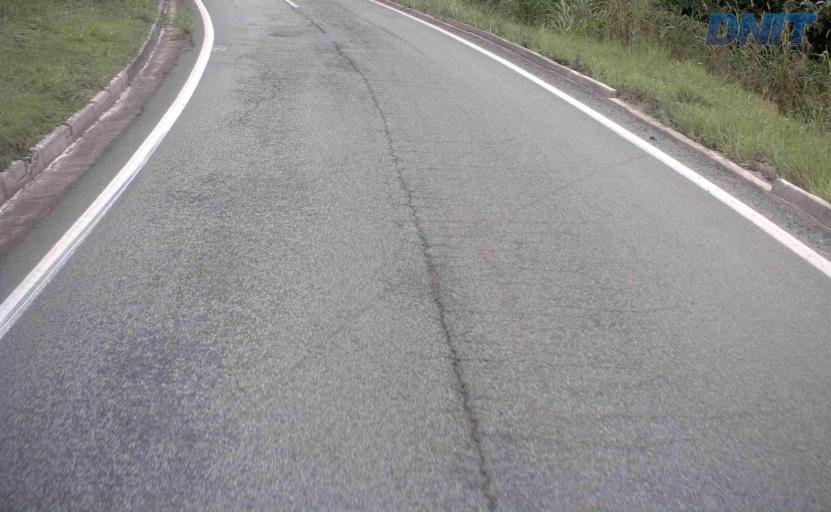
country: BR
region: Minas Gerais
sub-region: Timoteo
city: Timoteo
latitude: -19.6182
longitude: -42.8507
